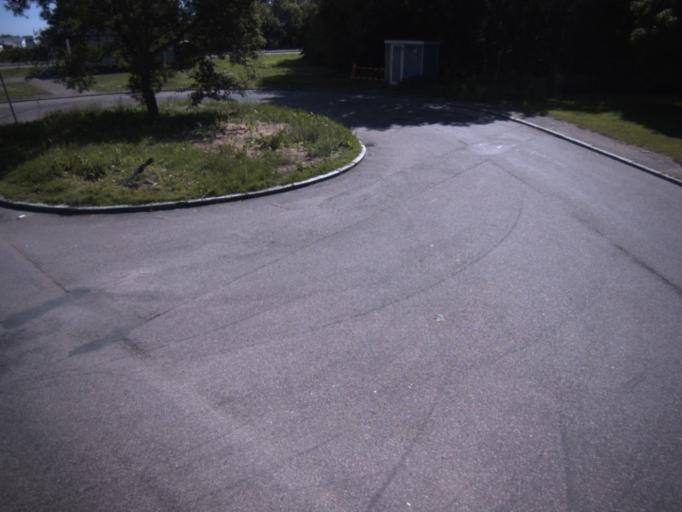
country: SE
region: Skane
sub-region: Helsingborg
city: Odakra
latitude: 56.0632
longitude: 12.7407
